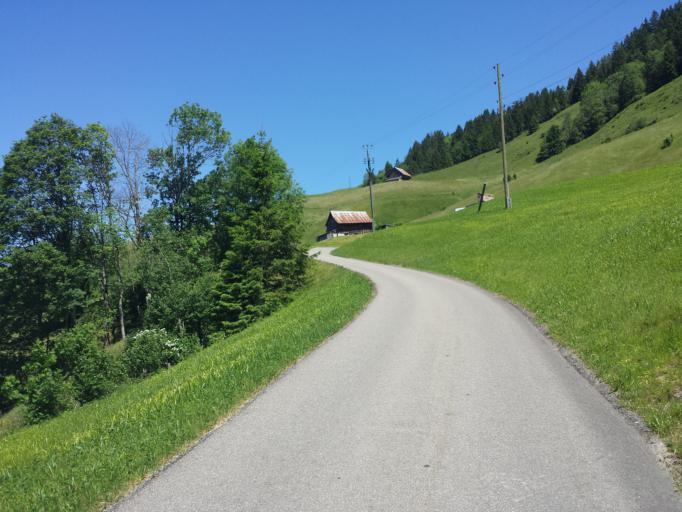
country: CH
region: Schwyz
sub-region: Bezirk March
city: Vorderthal
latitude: 47.0996
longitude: 8.9272
